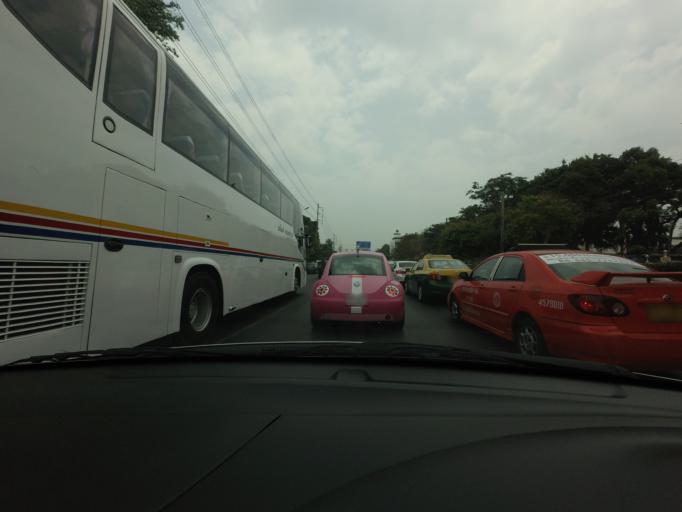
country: TH
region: Bangkok
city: Pom Prap Sattru Phai
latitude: 13.7591
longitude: 100.5185
